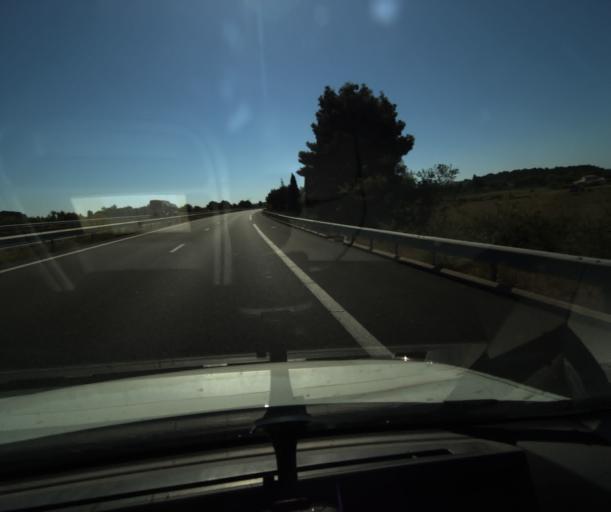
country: FR
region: Languedoc-Roussillon
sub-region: Departement de l'Aude
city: Fabrezan
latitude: 43.1730
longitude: 2.6905
